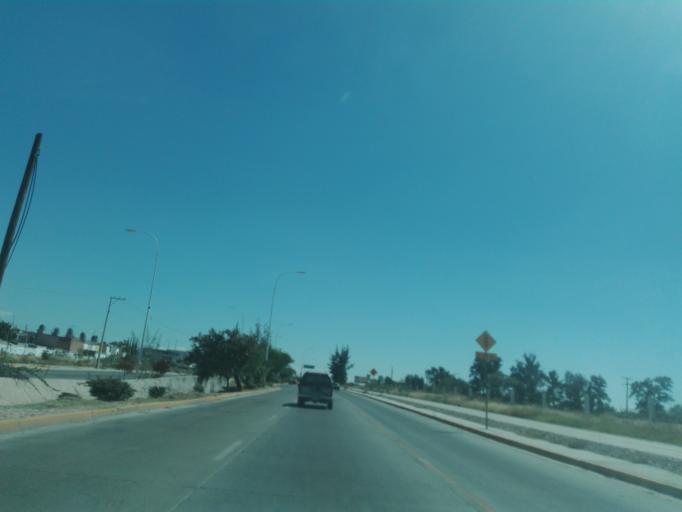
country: MX
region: Guanajuato
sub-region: Leon
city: San Jose de Duran (Los Troncoso)
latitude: 21.0772
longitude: -101.6537
